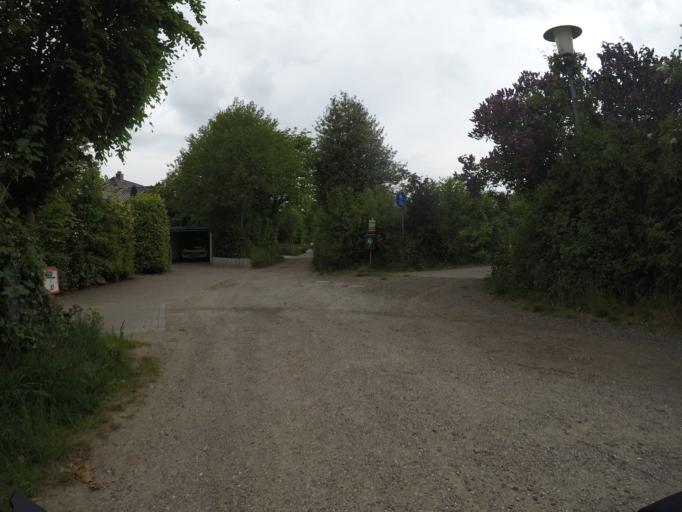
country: DE
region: Schleswig-Holstein
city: Kisdorf
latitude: 53.7864
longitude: 10.0113
